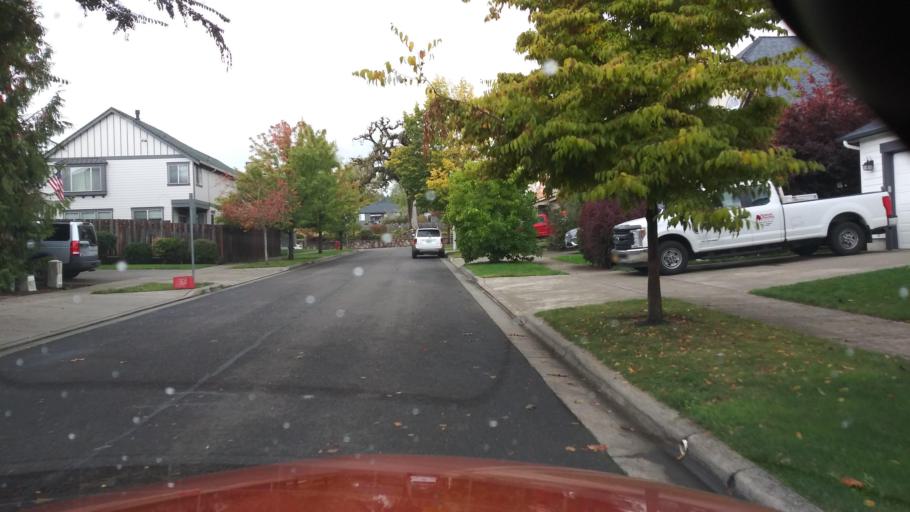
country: US
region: Oregon
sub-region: Washington County
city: Forest Grove
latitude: 45.5381
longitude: -123.1291
